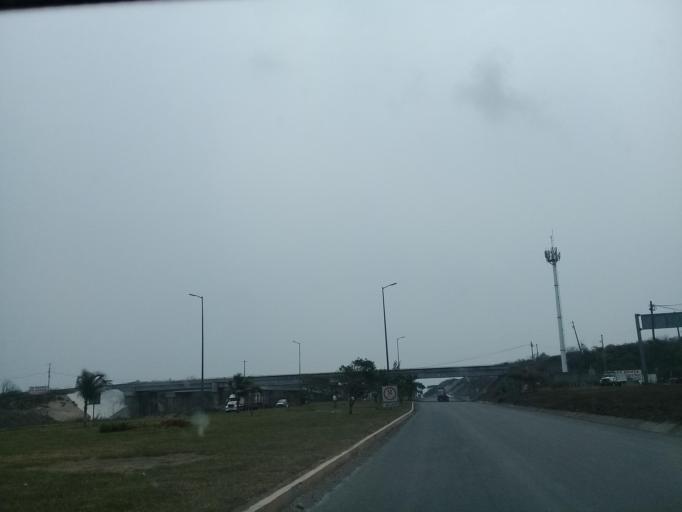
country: MX
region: Veracruz
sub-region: Veracruz
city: Colonia el Renacimiento
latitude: 19.2278
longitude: -96.2154
